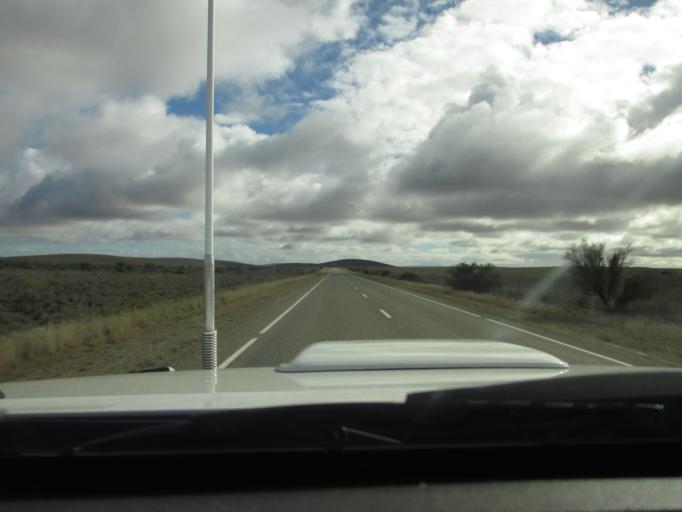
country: AU
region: South Australia
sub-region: Flinders Ranges
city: Quorn
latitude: -32.1710
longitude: 138.5360
